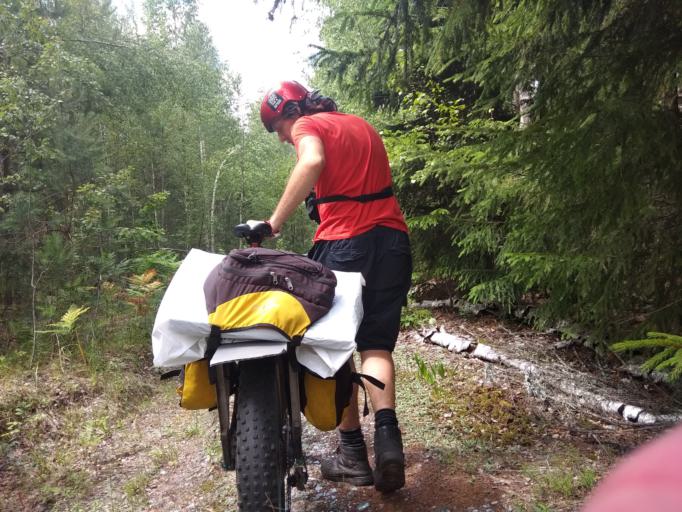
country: RU
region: Moskovskaya
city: Misheronskiy
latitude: 55.6456
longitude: 39.6970
